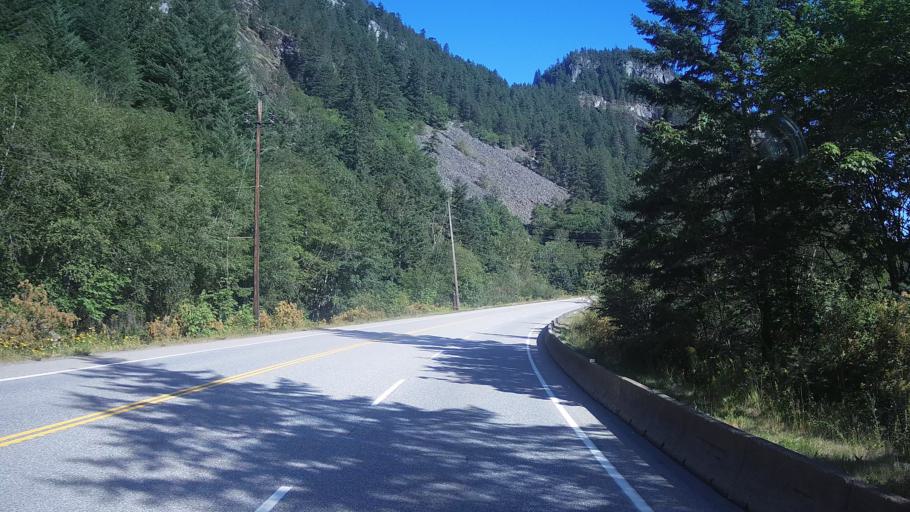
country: CA
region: British Columbia
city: Hope
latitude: 49.6403
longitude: -121.4094
